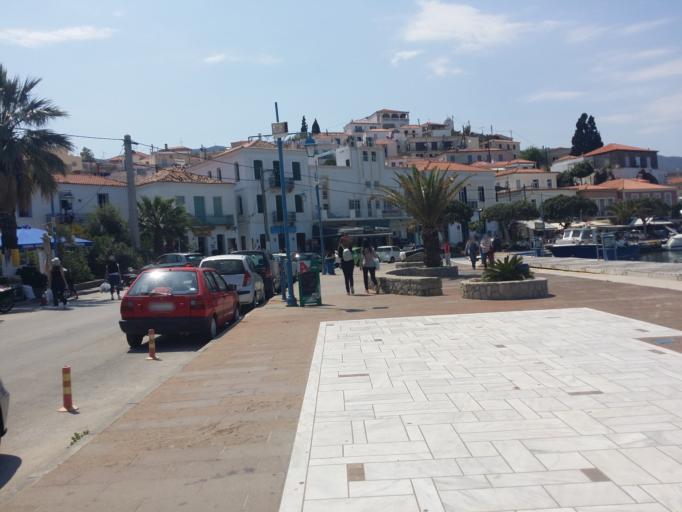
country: GR
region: Attica
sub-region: Nomos Piraios
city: Poros
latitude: 37.5020
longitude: 23.4547
